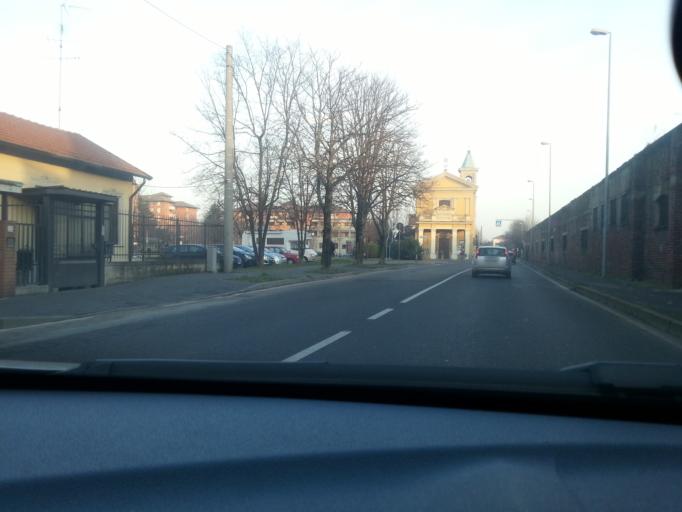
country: IT
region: Lombardy
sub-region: Citta metropolitana di Milano
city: Bollate
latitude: 45.5474
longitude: 9.1207
